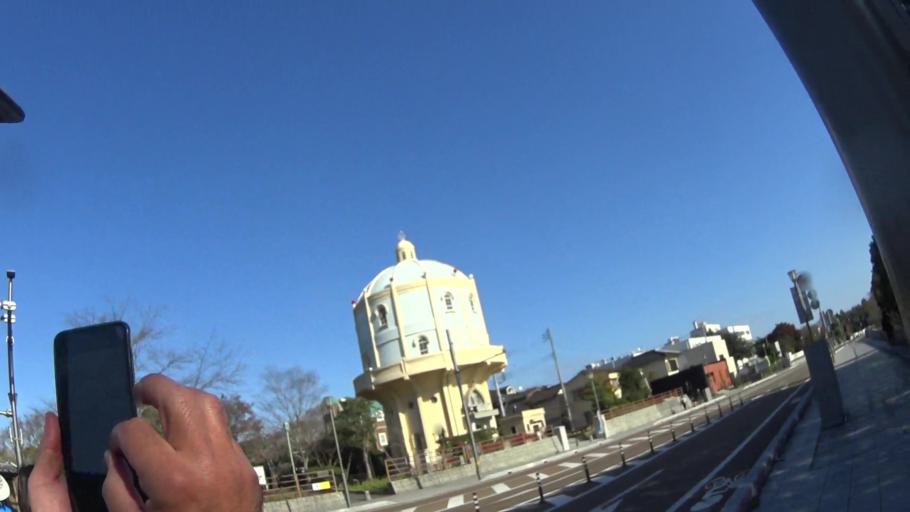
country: JP
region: Ibaraki
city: Mito-shi
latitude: 36.3777
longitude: 140.4750
